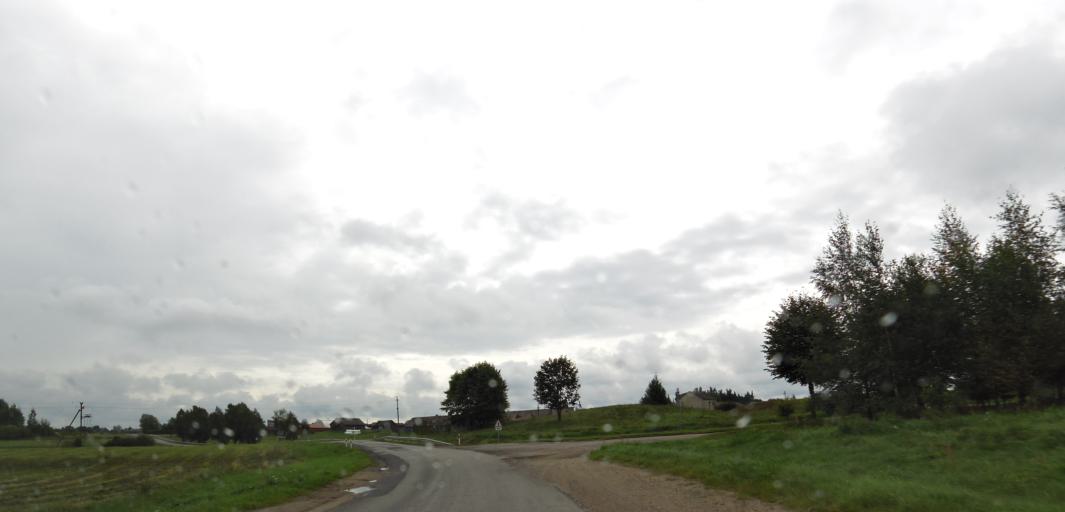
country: LT
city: Moletai
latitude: 55.2328
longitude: 25.3893
